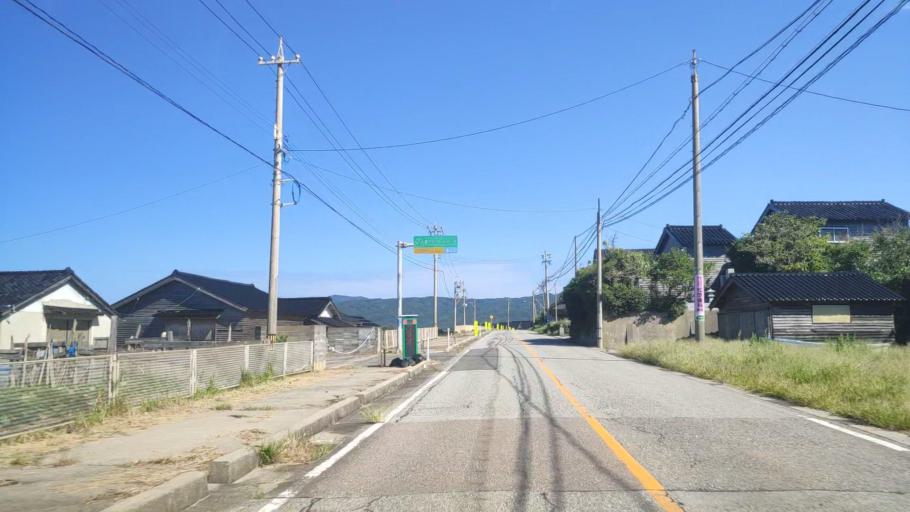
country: JP
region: Ishikawa
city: Nanao
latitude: 37.2734
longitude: 136.7320
